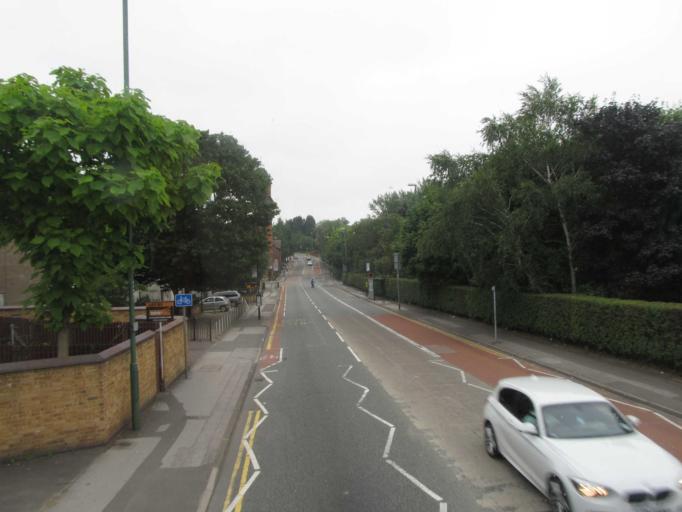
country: GB
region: England
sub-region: Nottingham
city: Nottingham
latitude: 52.9613
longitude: -1.1469
